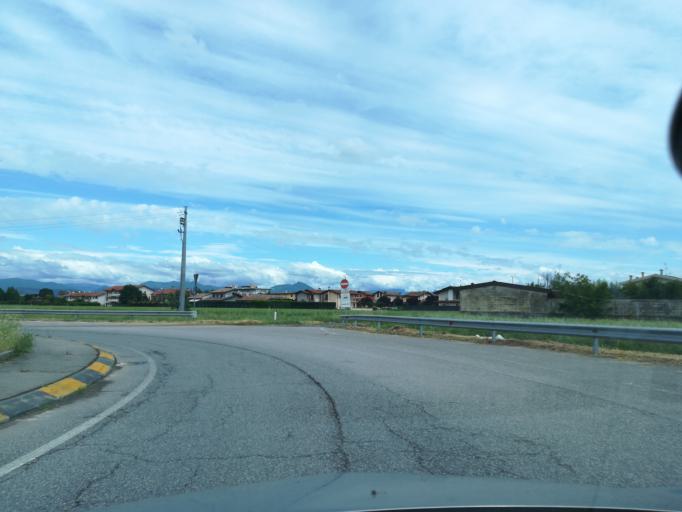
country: IT
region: Lombardy
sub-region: Provincia di Bergamo
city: Cividate al Piano
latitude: 45.5551
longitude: 9.8227
